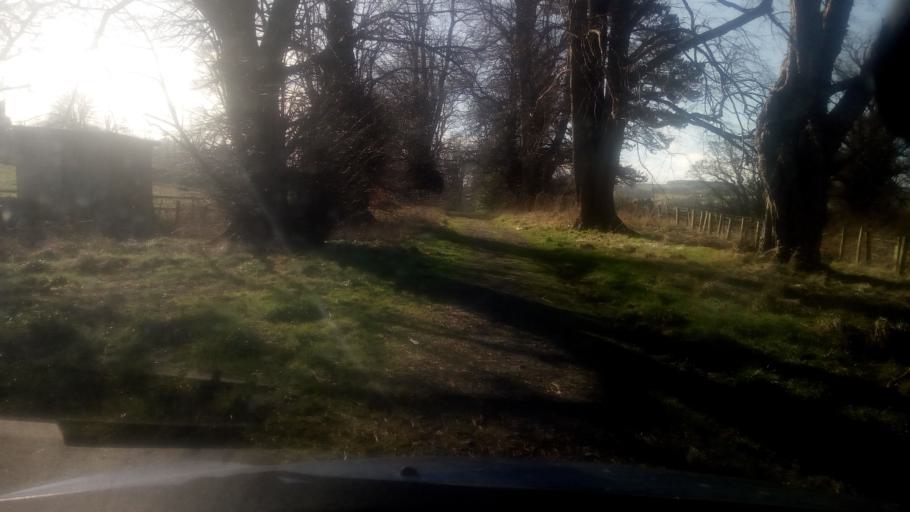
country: GB
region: Scotland
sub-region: The Scottish Borders
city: Jedburgh
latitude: 55.4818
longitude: -2.5420
